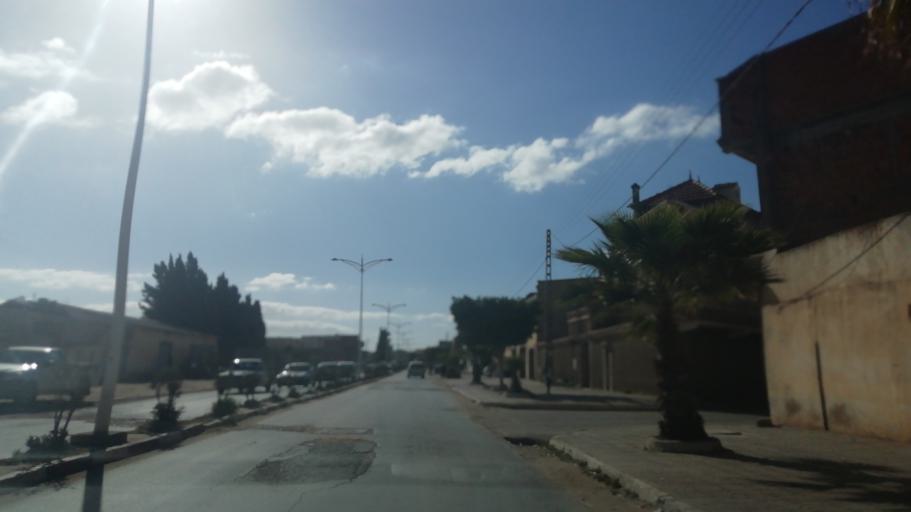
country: DZ
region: Mostaganem
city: Mostaganem
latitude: 35.9948
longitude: 0.2991
